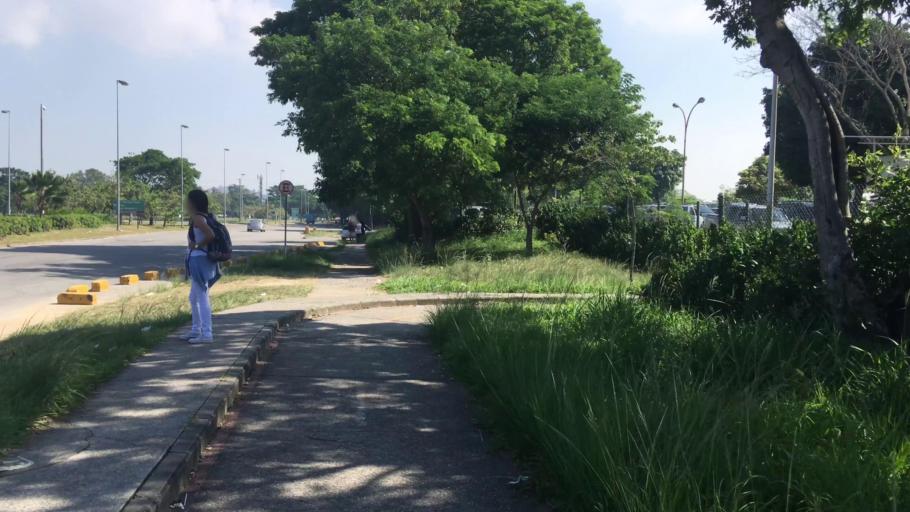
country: BR
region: Rio de Janeiro
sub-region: Rio De Janeiro
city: Rio de Janeiro
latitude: -22.8432
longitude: -43.2336
